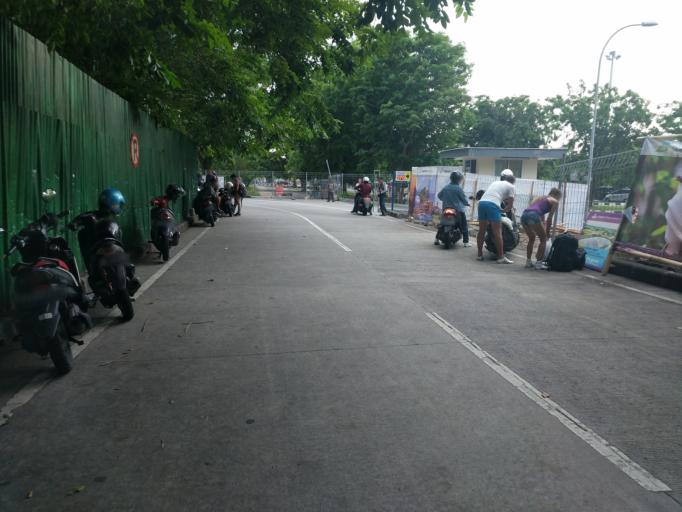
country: ID
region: Bali
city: Jabajero
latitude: -8.7404
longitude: 115.1640
